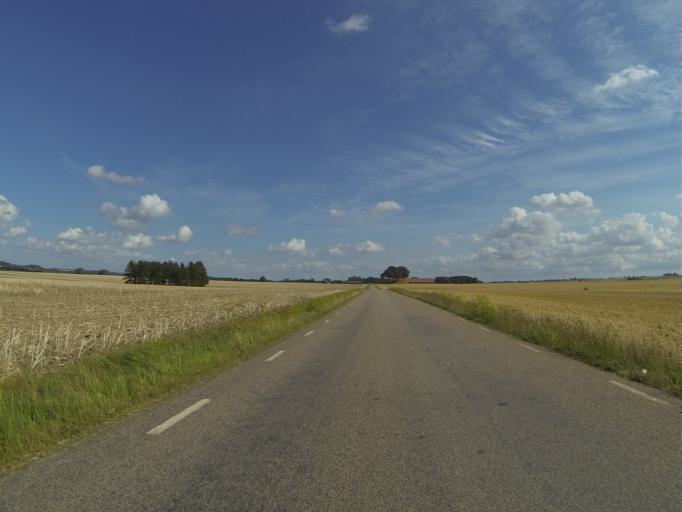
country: SE
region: Skane
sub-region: Lunds Kommun
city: Lund
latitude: 55.7714
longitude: 13.2391
